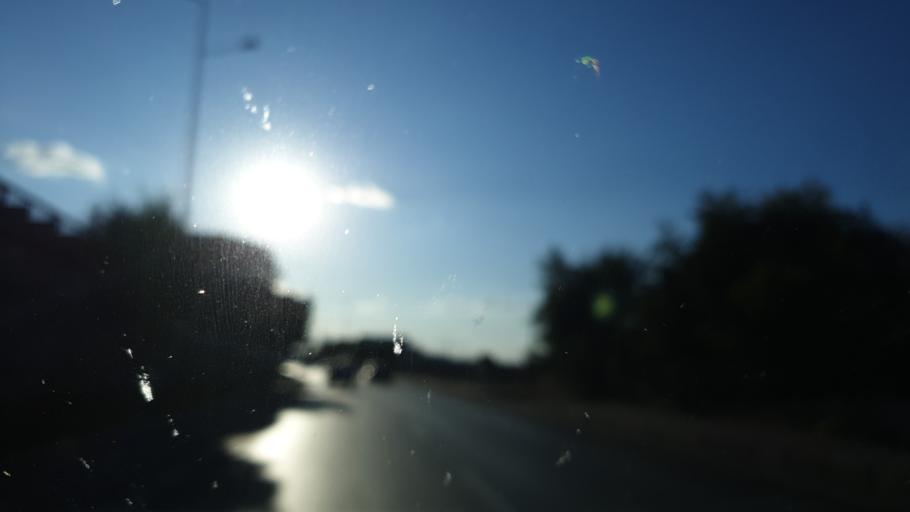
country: TR
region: Kayseri
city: Kocasinan
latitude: 38.7500
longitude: 35.5481
